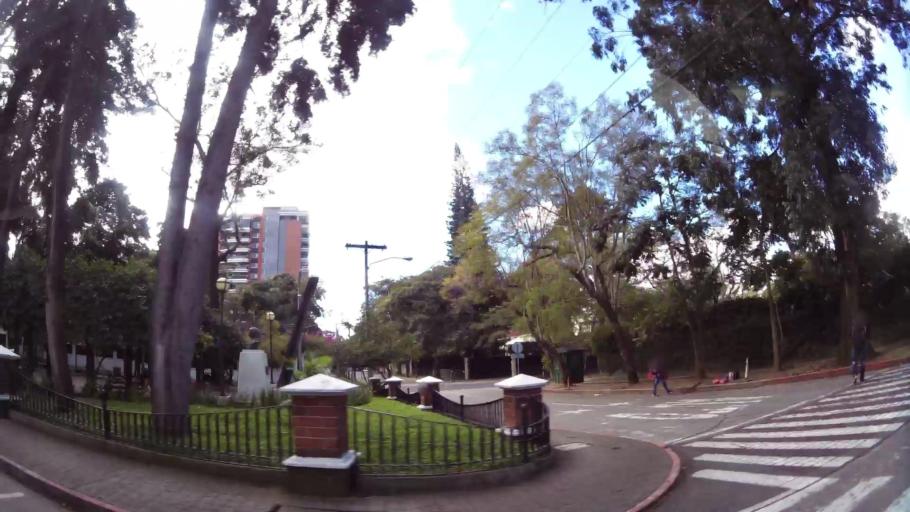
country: GT
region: Guatemala
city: Santa Catarina Pinula
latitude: 14.5976
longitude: -90.5101
